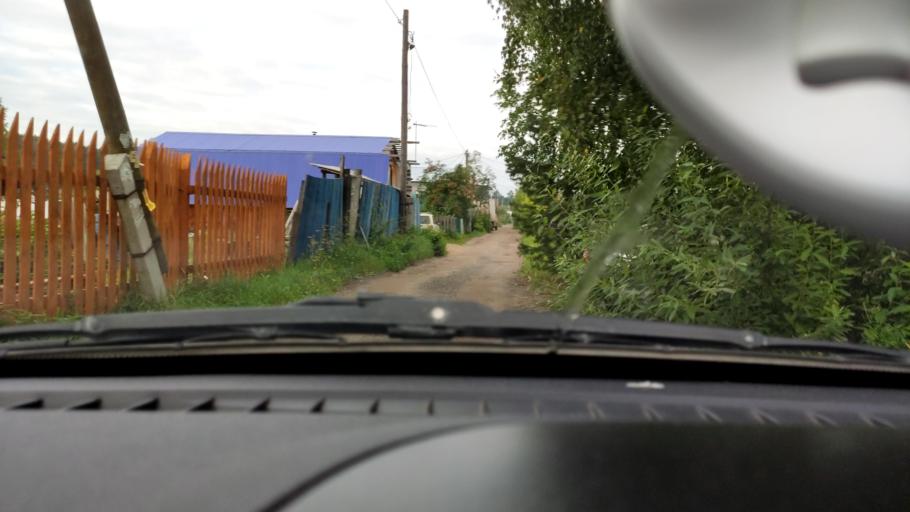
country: RU
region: Perm
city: Overyata
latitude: 58.0185
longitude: 55.9648
